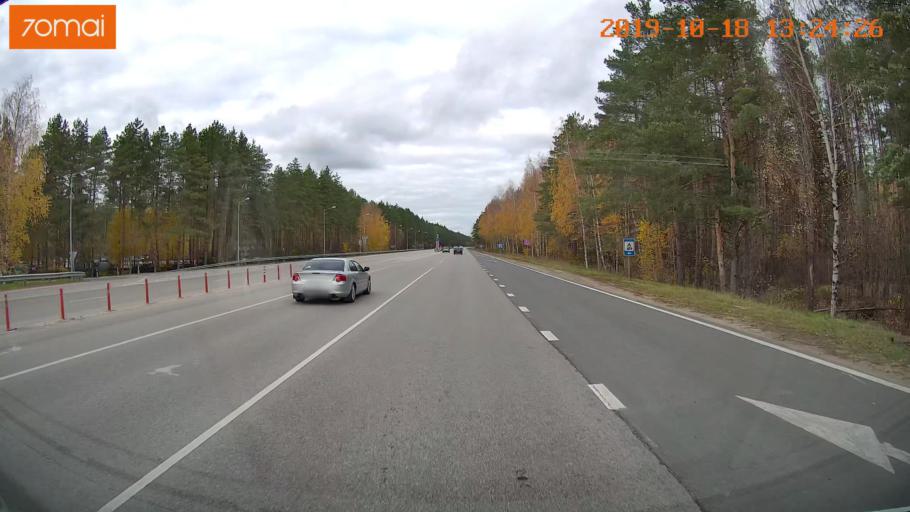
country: RU
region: Rjazan
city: Polyany
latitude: 54.7306
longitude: 39.8440
